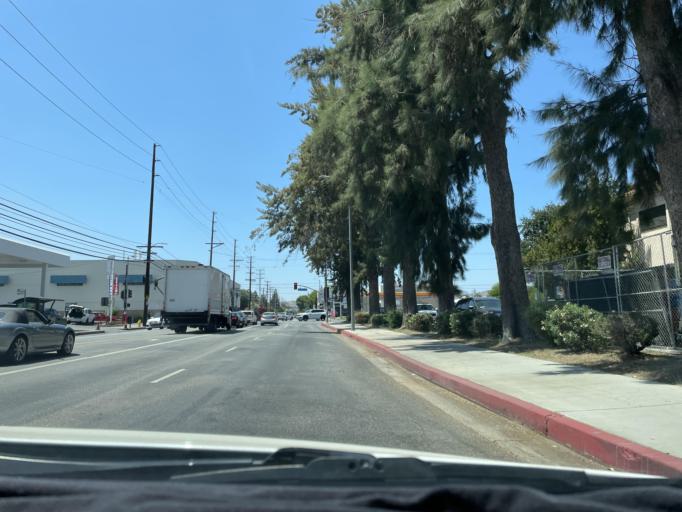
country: US
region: California
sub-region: Los Angeles County
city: Canoga Park
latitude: 34.1938
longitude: -118.6050
